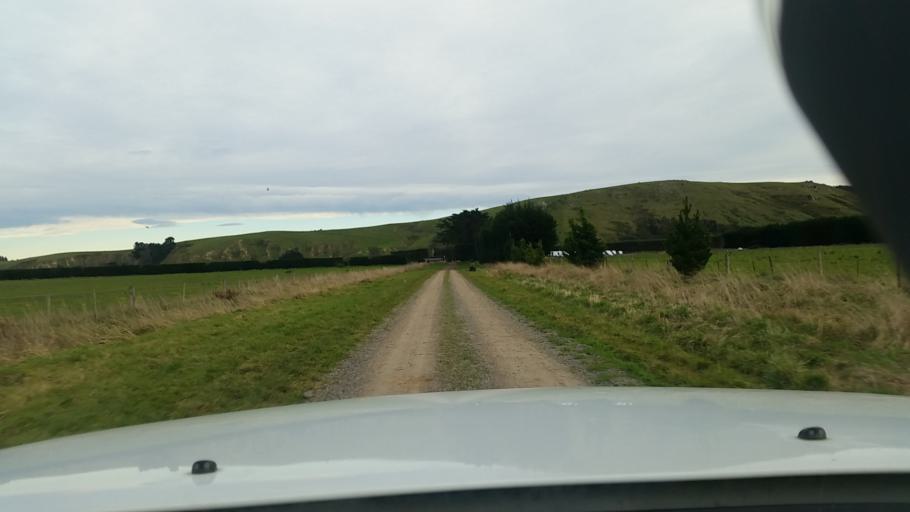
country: NZ
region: Canterbury
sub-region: Selwyn District
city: Lincoln
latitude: -43.7208
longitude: 172.6107
